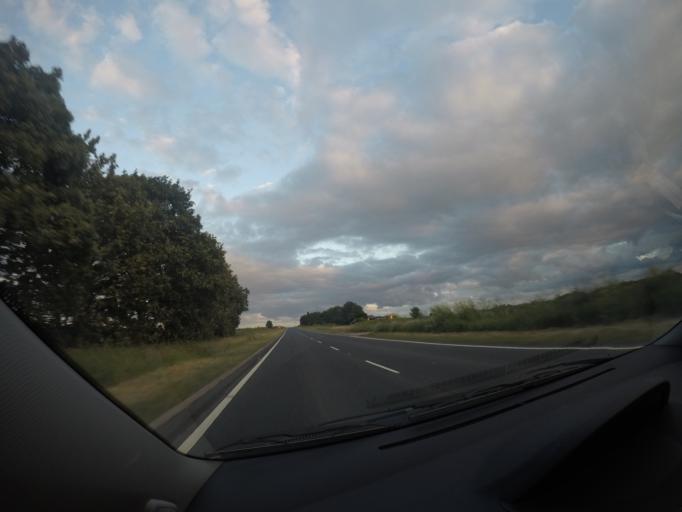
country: GB
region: England
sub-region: North Yorkshire
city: Bedale
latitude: 54.2447
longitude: -1.5040
